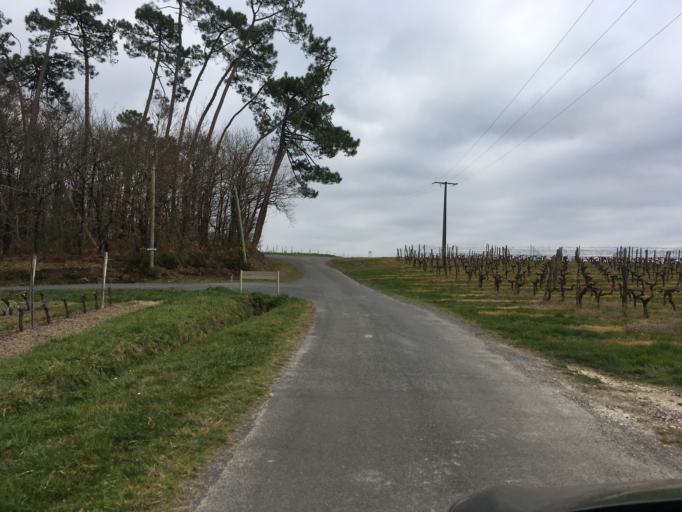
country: FR
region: Aquitaine
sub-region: Departement de la Gironde
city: Saint-Ciers-sur-Gironde
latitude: 45.3188
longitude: -0.6023
